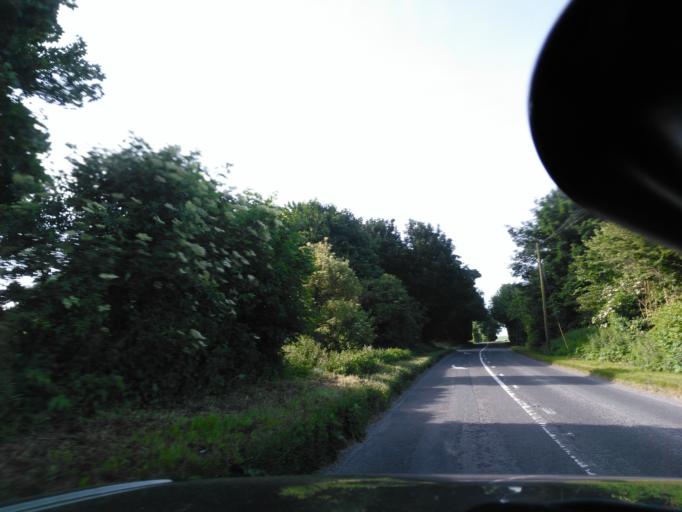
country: GB
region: England
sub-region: Wiltshire
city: Market Lavington
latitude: 51.2576
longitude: -1.9881
